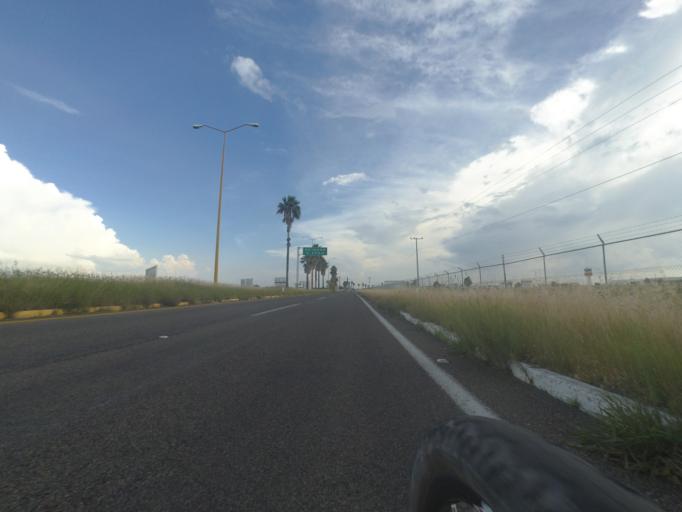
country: MX
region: Aguascalientes
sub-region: Aguascalientes
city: Penuelas (El Cienegal)
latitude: 21.7070
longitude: -102.3110
